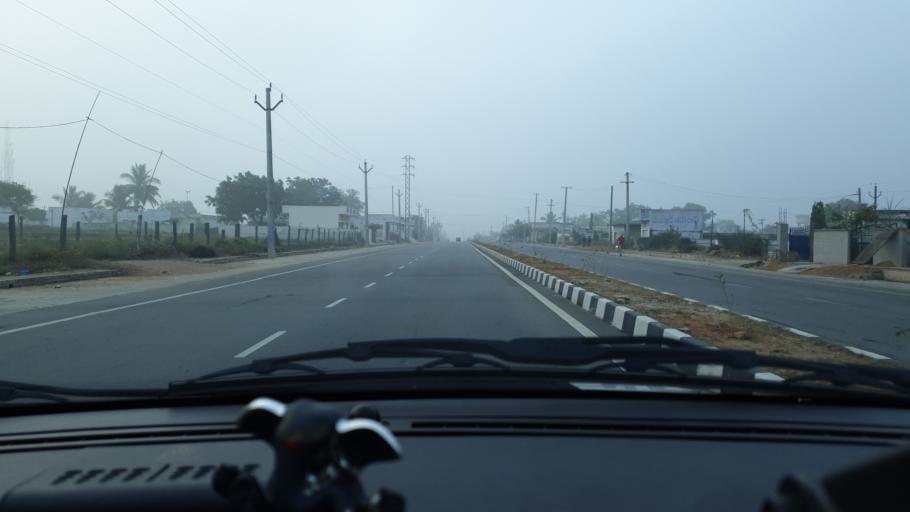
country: IN
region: Telangana
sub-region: Mahbubnagar
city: Farrukhnagar
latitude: 16.8847
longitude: 78.5290
